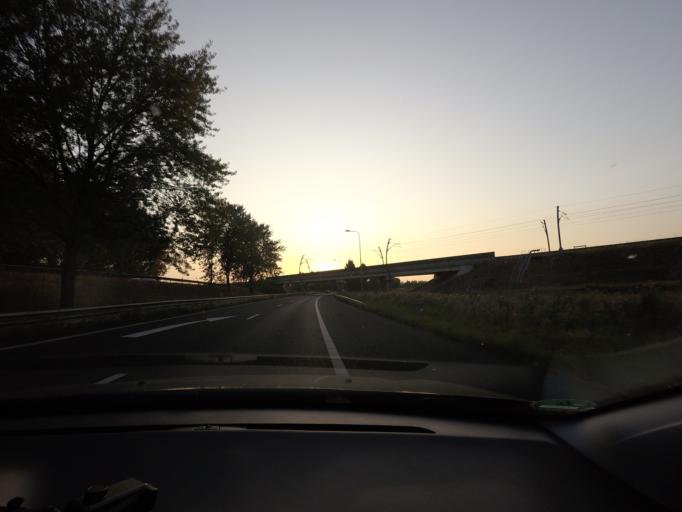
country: NL
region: Gelderland
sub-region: Gemeente Zaltbommel
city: Zaltbommel
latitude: 51.8589
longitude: 5.2305
